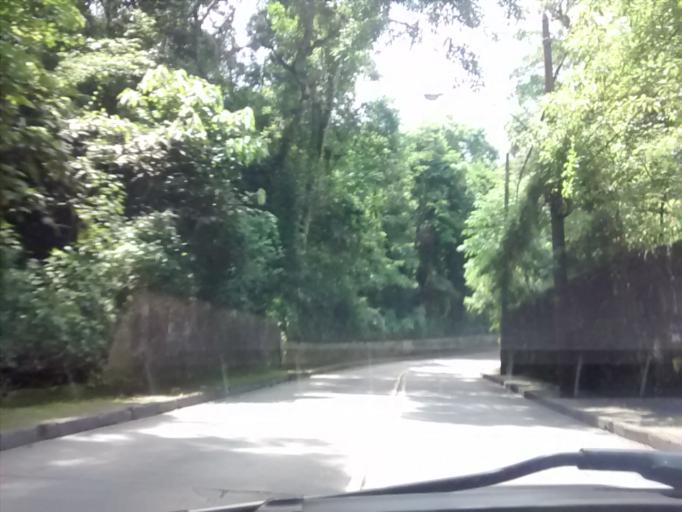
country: BR
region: Rio de Janeiro
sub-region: Rio De Janeiro
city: Rio de Janeiro
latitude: -22.9741
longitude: -43.2805
